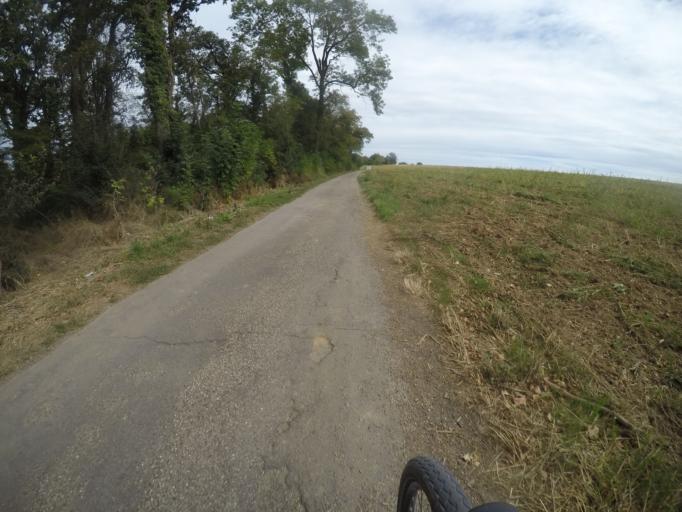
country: DE
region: Baden-Wuerttemberg
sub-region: Karlsruhe Region
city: Muhlacker
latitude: 48.9330
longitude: 8.8100
